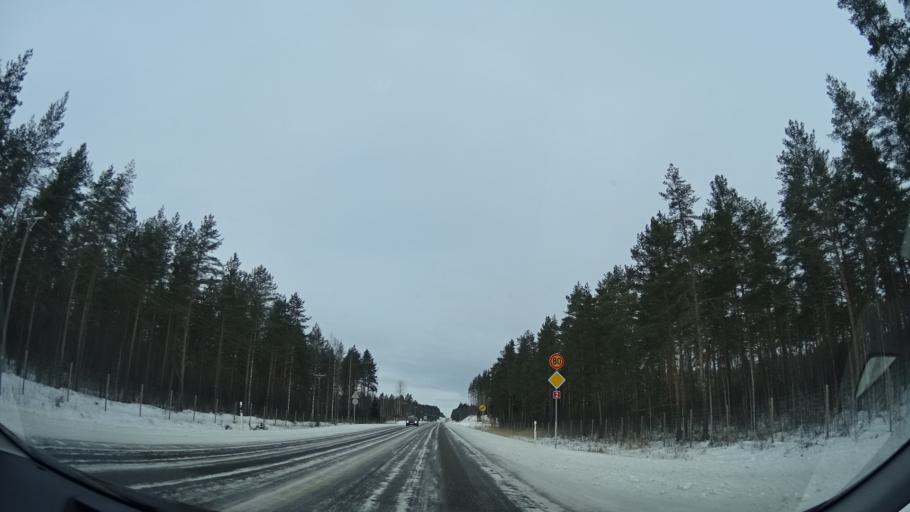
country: FI
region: Uusimaa
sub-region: Helsinki
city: Kaerkoelae
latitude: 60.6470
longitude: 23.8716
